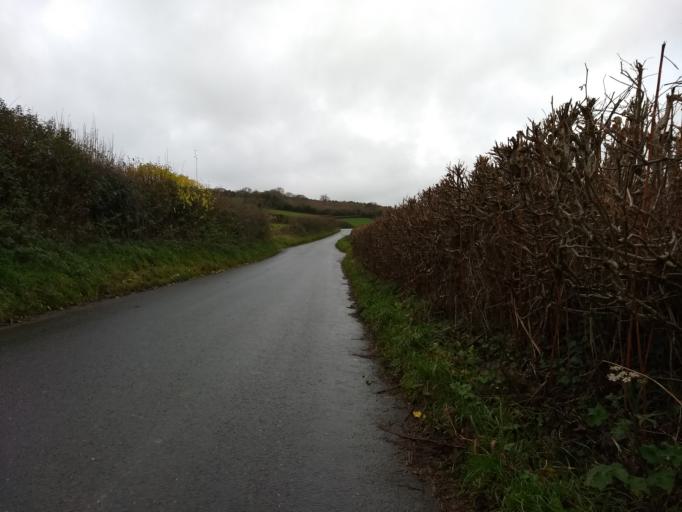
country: GB
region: England
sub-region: Isle of Wight
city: Newport
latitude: 50.6887
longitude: -1.2722
